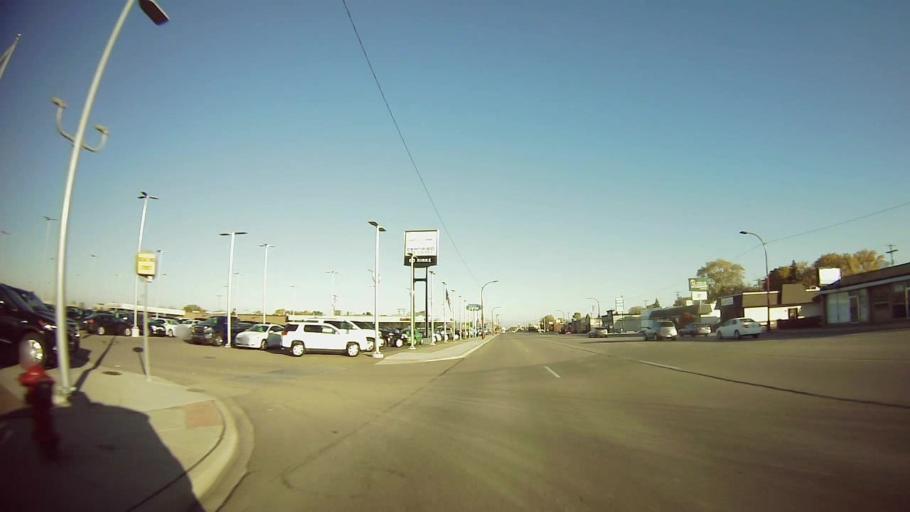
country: US
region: Michigan
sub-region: Macomb County
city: Center Line
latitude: 42.4863
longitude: -83.0277
